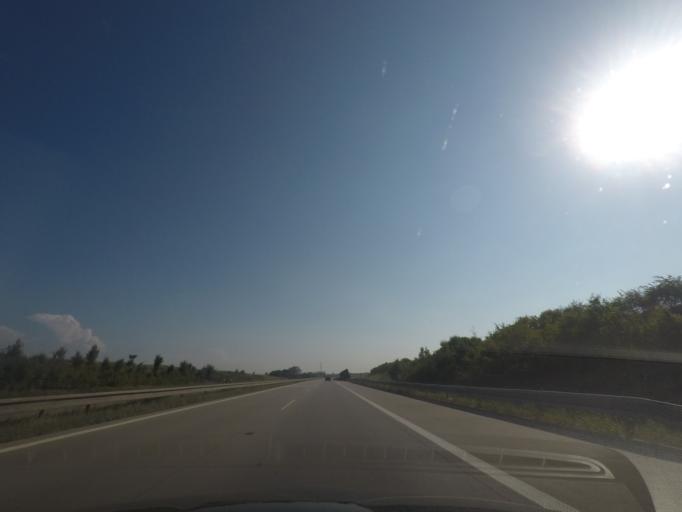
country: CZ
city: Bilovec
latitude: 49.7161
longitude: 18.0039
